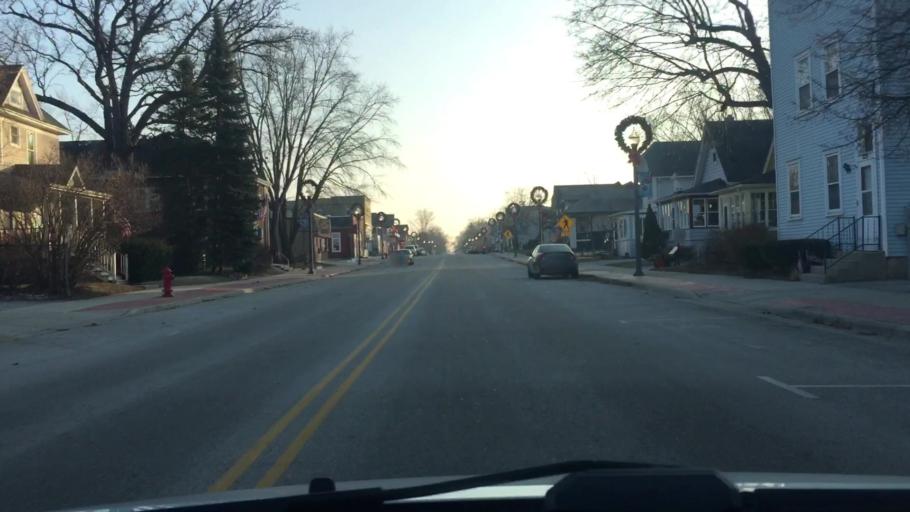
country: US
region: Wisconsin
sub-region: Waukesha County
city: Dousman
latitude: 43.0167
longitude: -88.4728
